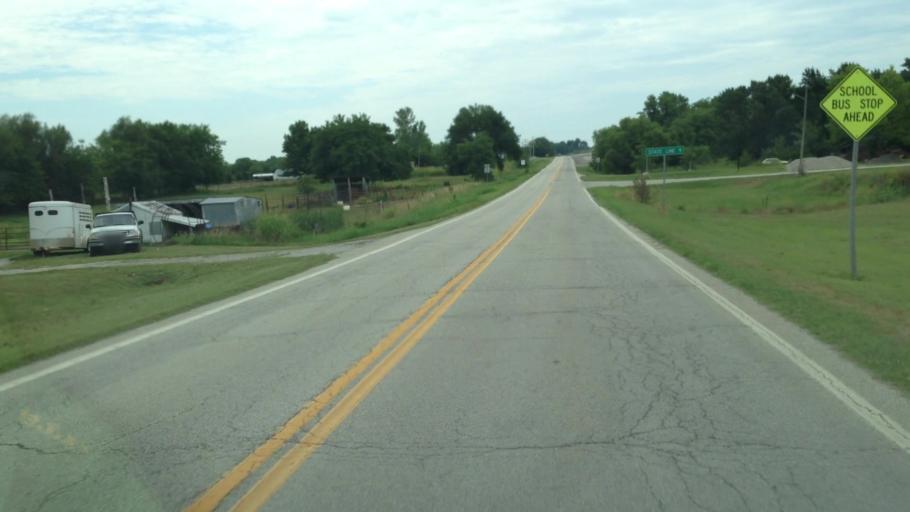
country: US
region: Kansas
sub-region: Labette County
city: Chetopa
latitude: 36.8756
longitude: -95.0989
